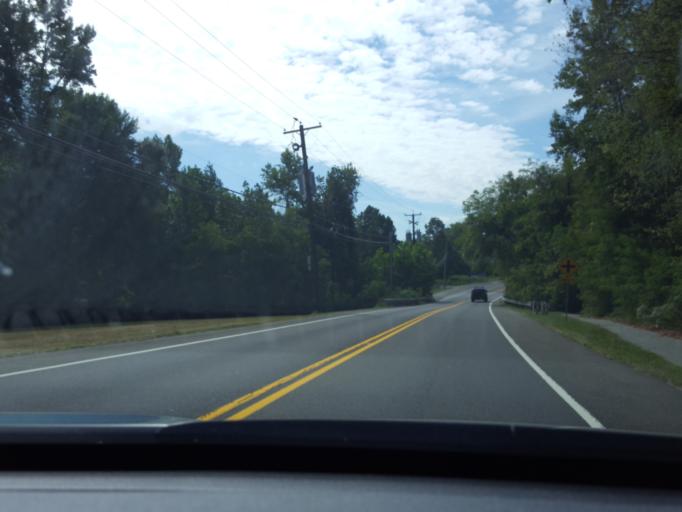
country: US
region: Maryland
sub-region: Prince George's County
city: Mellwood
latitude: 38.8021
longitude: -76.8250
